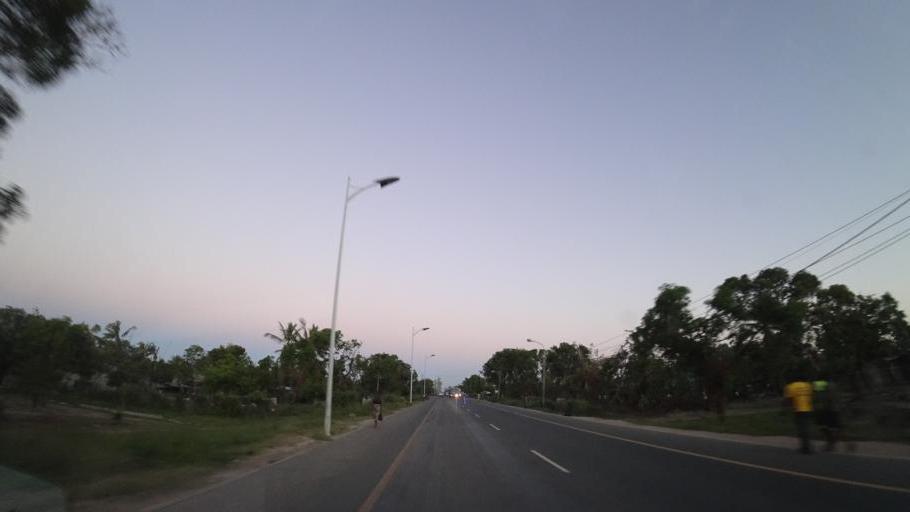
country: MZ
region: Sofala
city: Dondo
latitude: -19.5411
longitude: 34.6382
